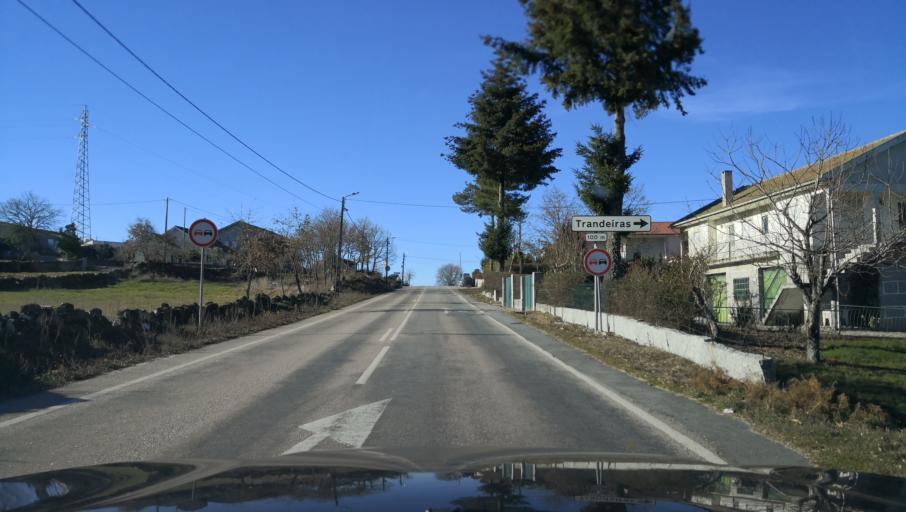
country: PT
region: Vila Real
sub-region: Vila Pouca de Aguiar
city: Vila Pouca de Aguiar
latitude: 41.5005
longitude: -7.6864
